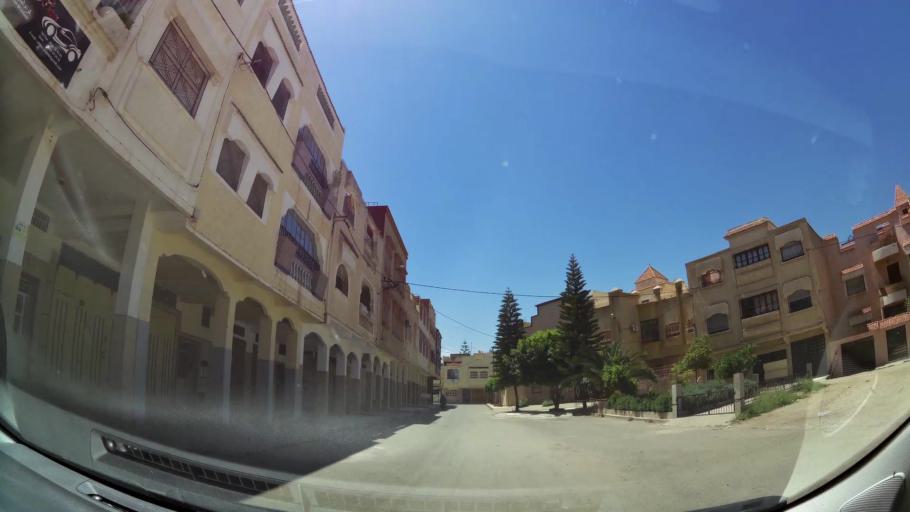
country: MA
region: Oriental
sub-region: Oujda-Angad
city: Oujda
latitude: 34.6669
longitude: -1.8900
